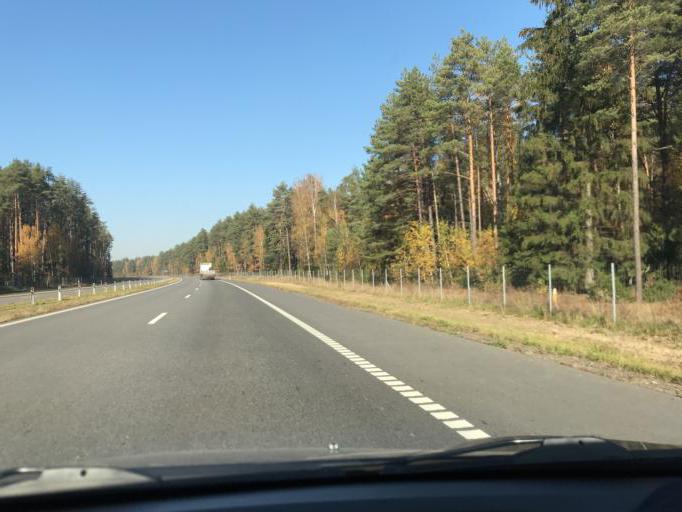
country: BY
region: Mogilev
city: Kirawsk
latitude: 53.2231
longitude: 29.3389
